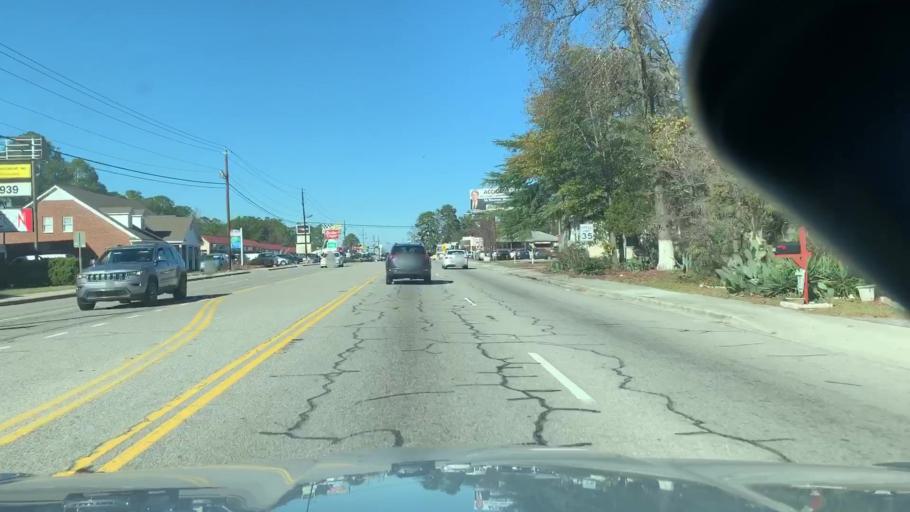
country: US
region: South Carolina
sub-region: Richland County
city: Woodfield
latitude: 34.0474
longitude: -80.9433
